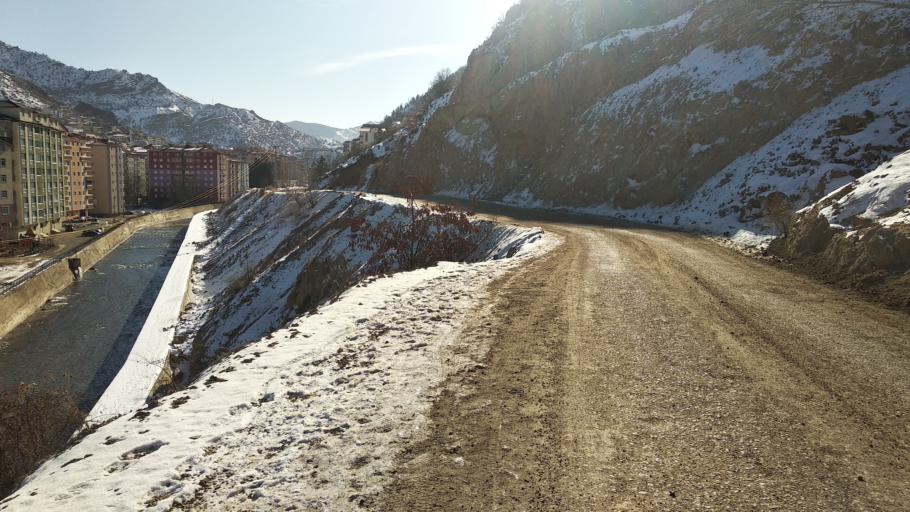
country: TR
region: Gumushane
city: Gumushkhane
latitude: 40.4539
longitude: 39.4893
